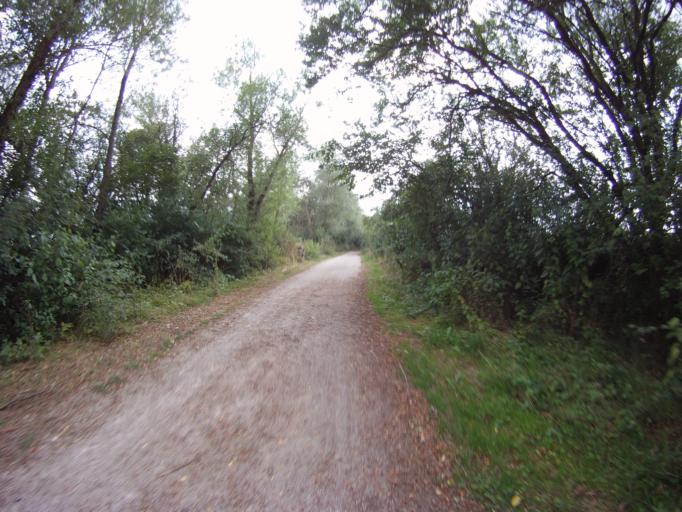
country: FR
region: Lorraine
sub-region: Departement de la Moselle
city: Retonfey
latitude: 49.0736
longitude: 6.3312
